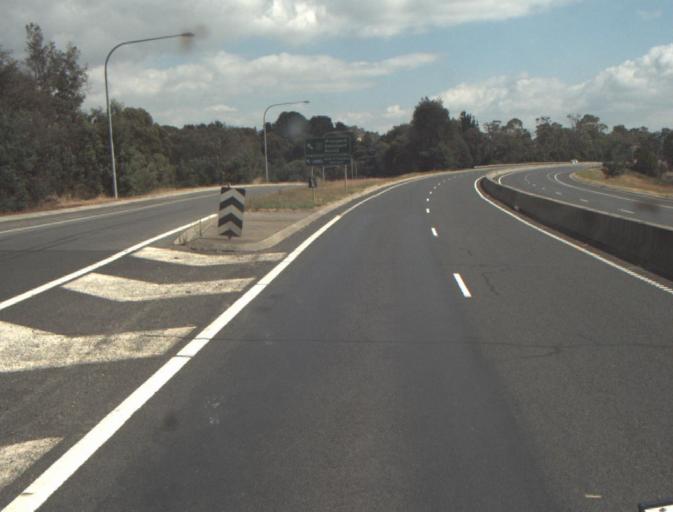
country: AU
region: Tasmania
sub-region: Launceston
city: Summerhill
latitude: -41.4747
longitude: 147.1433
